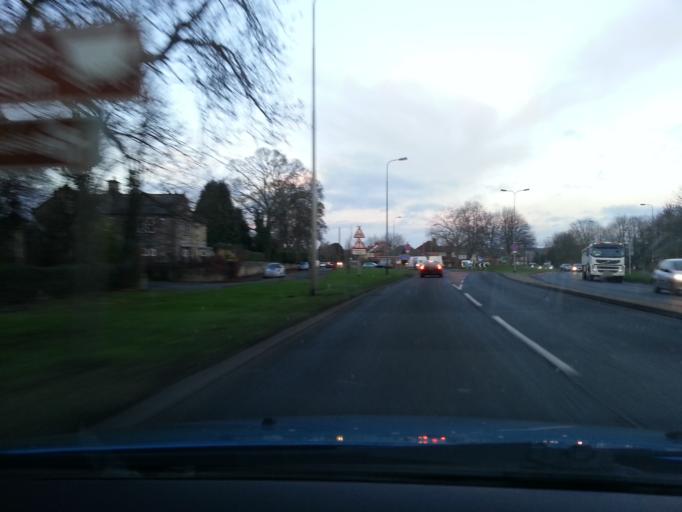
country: GB
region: England
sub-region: County Durham
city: Chester-le-Street
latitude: 54.8447
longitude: -1.5753
